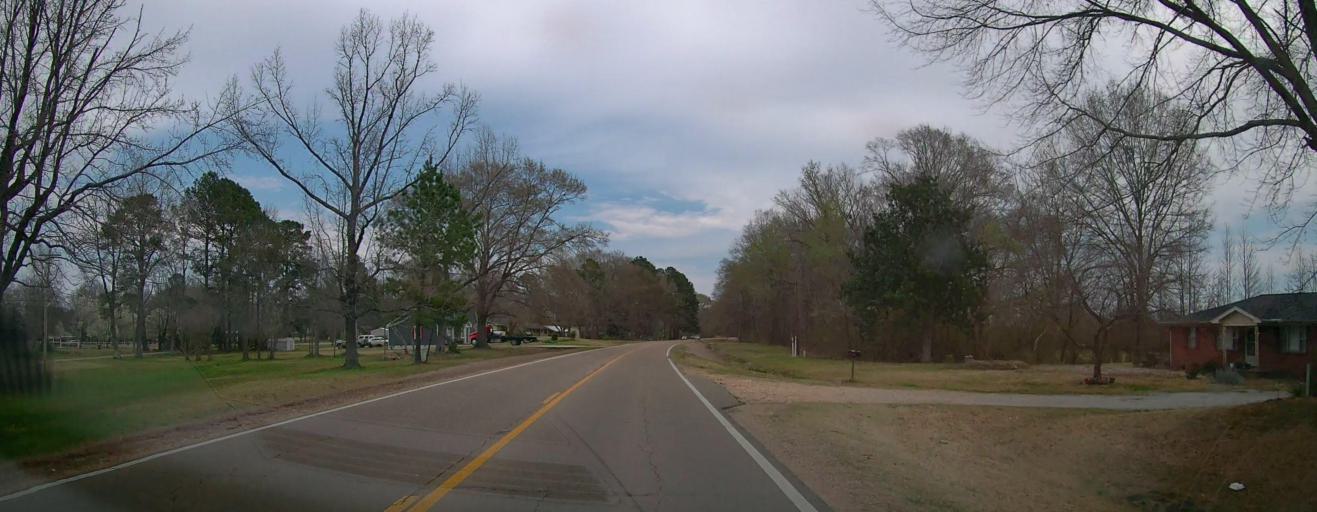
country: US
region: Mississippi
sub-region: Lee County
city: Plantersville
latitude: 34.2651
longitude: -88.6374
